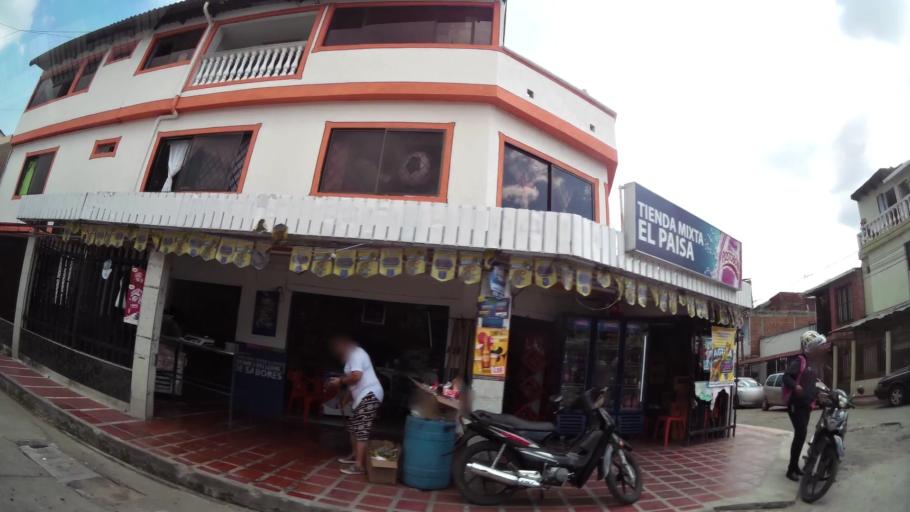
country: CO
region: Valle del Cauca
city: Cali
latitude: 3.4150
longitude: -76.5200
